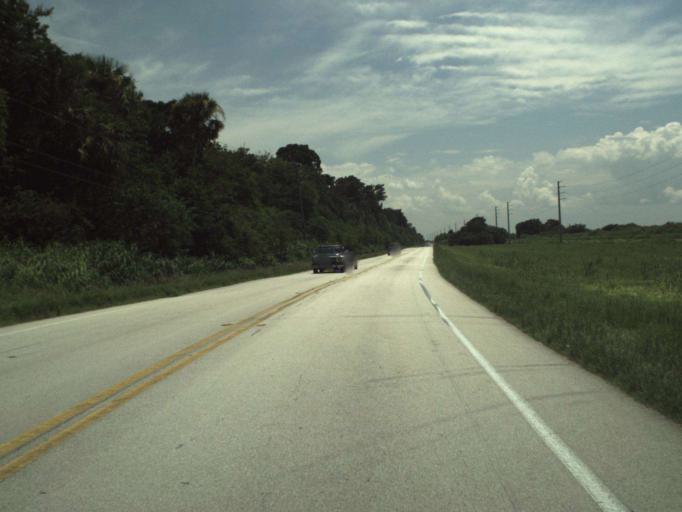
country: US
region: Florida
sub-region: Palm Beach County
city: Pahokee
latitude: 26.9431
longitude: -80.6097
